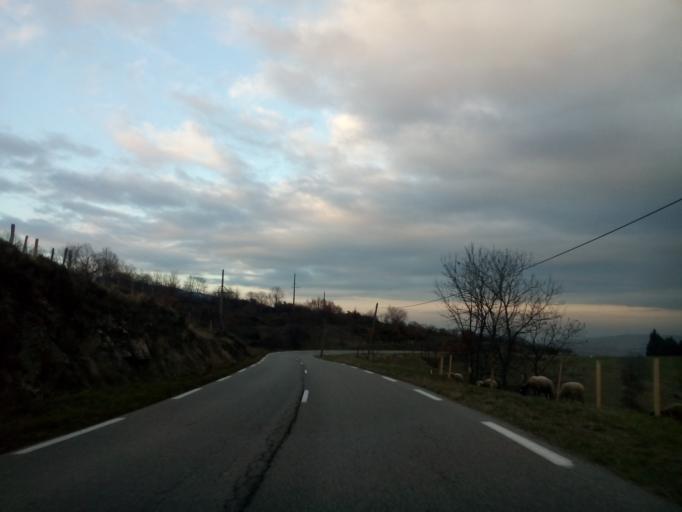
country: FR
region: Rhone-Alpes
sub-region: Departement de la Loire
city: Saint-Julien-Molin-Molette
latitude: 45.3342
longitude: 4.6423
